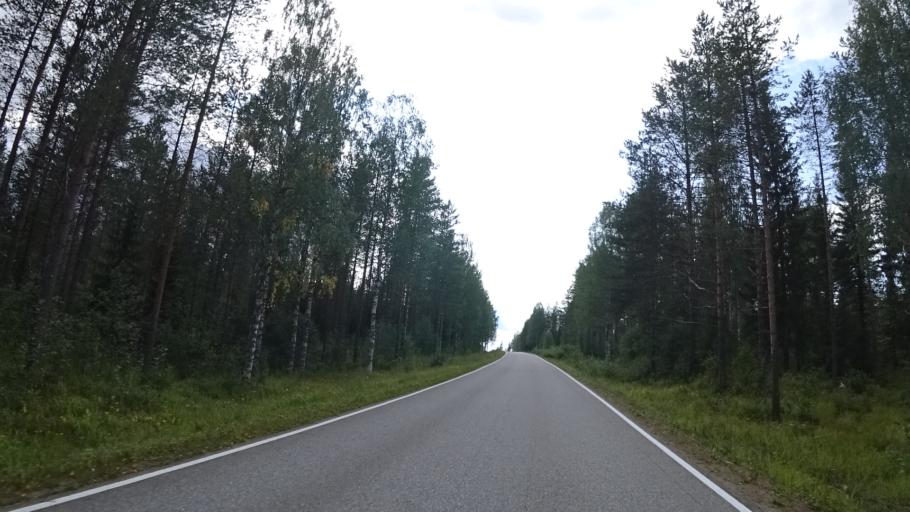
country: FI
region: North Karelia
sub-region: Joensuu
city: Ilomantsi
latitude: 62.4217
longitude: 31.0248
